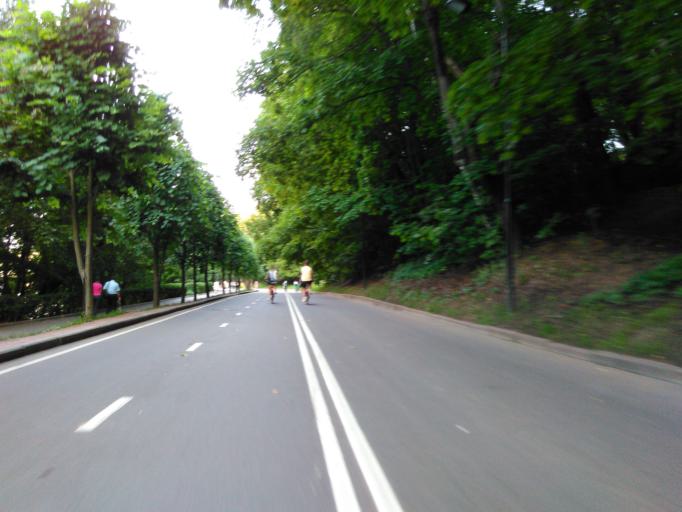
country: RU
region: Moscow
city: Luzhniki
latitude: 55.7109
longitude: 37.5480
